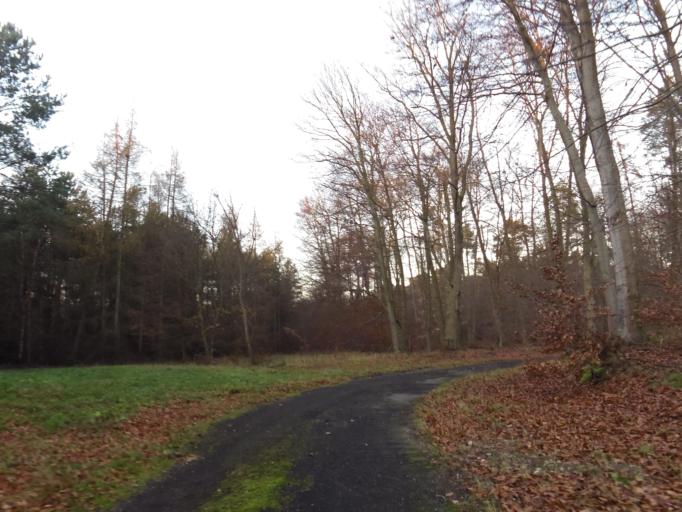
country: DE
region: Hesse
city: Morfelden-Walldorf
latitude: 49.9983
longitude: 8.6071
